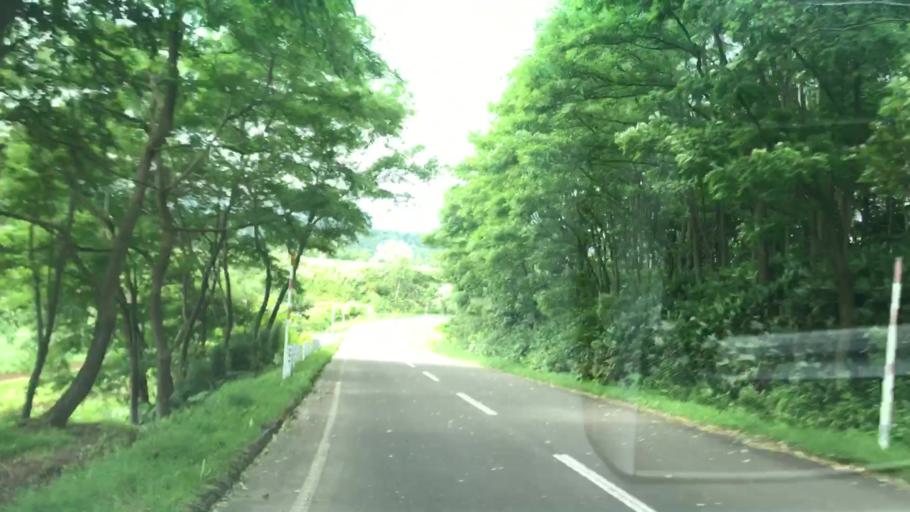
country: JP
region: Hokkaido
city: Niseko Town
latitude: 42.9137
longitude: 140.7594
